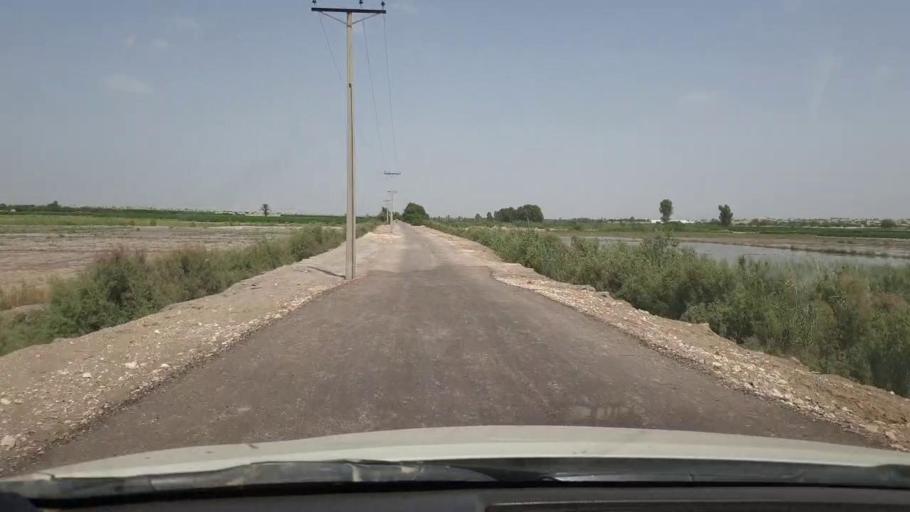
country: PK
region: Sindh
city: Rohri
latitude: 27.4824
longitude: 69.0565
